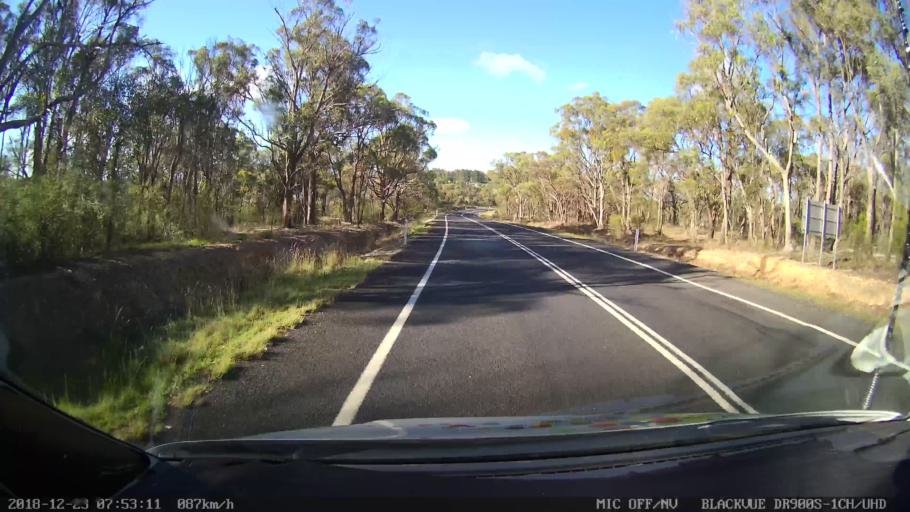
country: AU
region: New South Wales
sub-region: Armidale Dumaresq
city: Armidale
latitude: -30.5347
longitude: 151.8116
